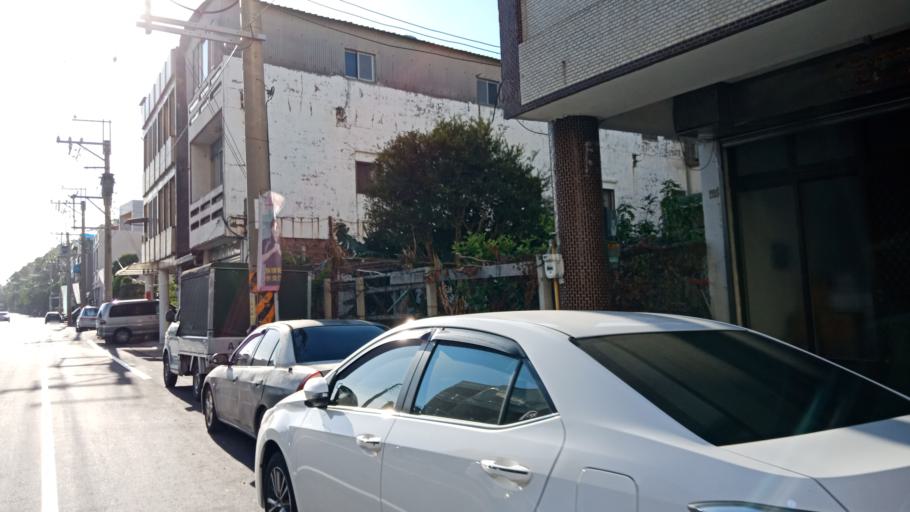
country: TW
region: Taiwan
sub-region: Miaoli
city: Miaoli
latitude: 24.4944
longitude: 120.6885
